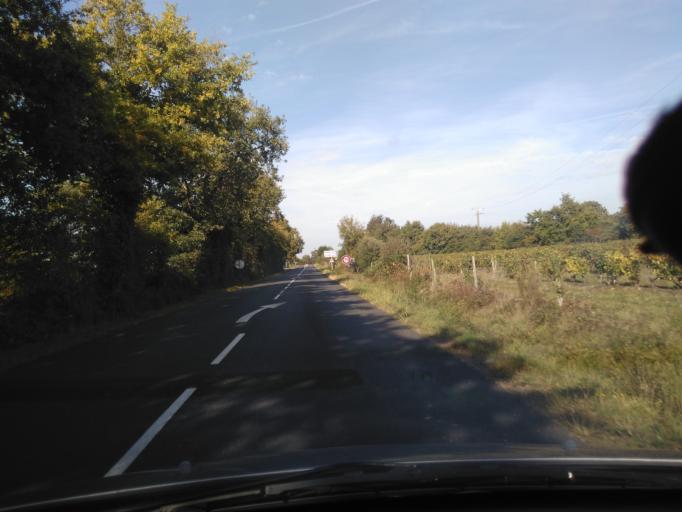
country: FR
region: Pays de la Loire
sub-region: Departement de la Vendee
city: Grosbreuil
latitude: 46.5224
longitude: -1.5543
